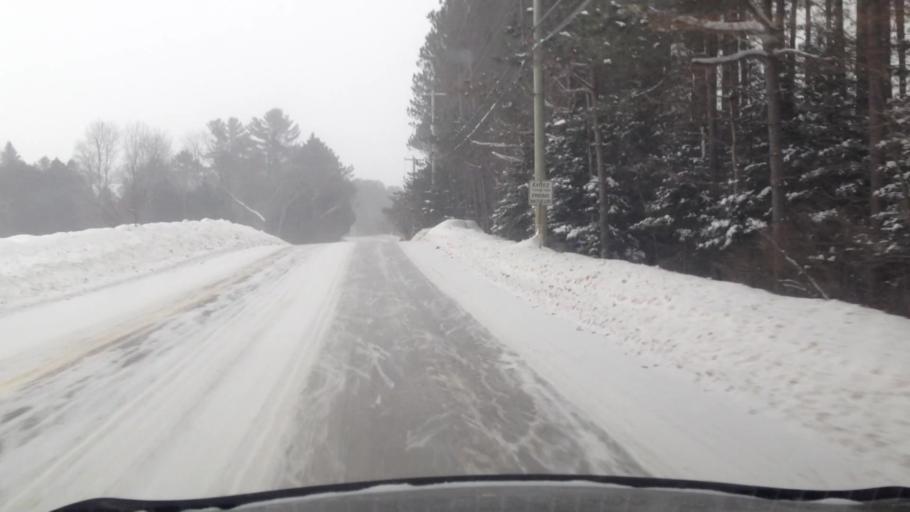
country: CA
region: Quebec
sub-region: Laurentides
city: Mont-Tremblant
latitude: 45.9675
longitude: -74.6270
